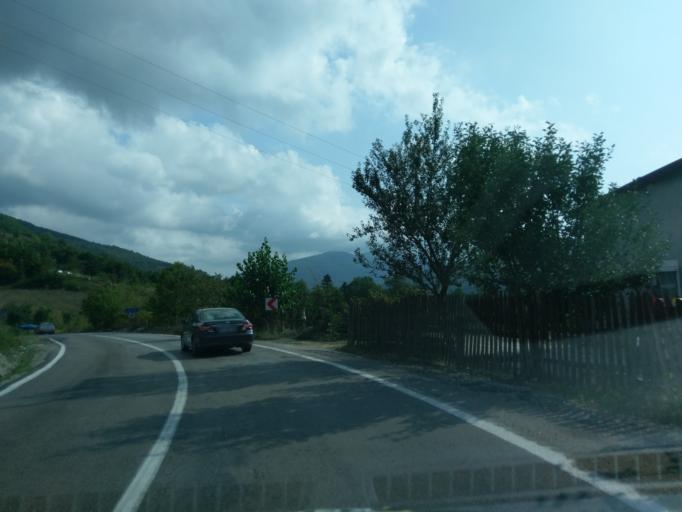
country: TR
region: Sinop
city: Yenikonak
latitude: 41.8764
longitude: 34.5425
